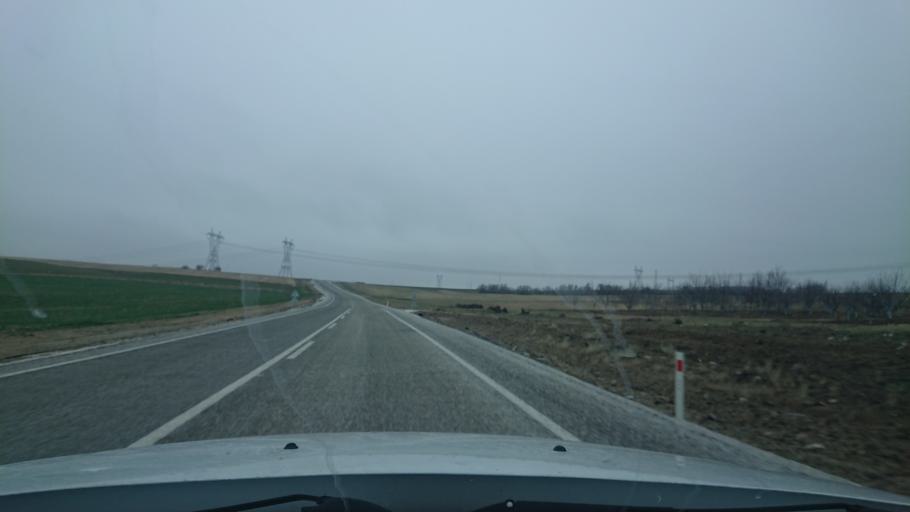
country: TR
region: Aksaray
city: Agacoren
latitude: 38.9016
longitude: 33.9333
